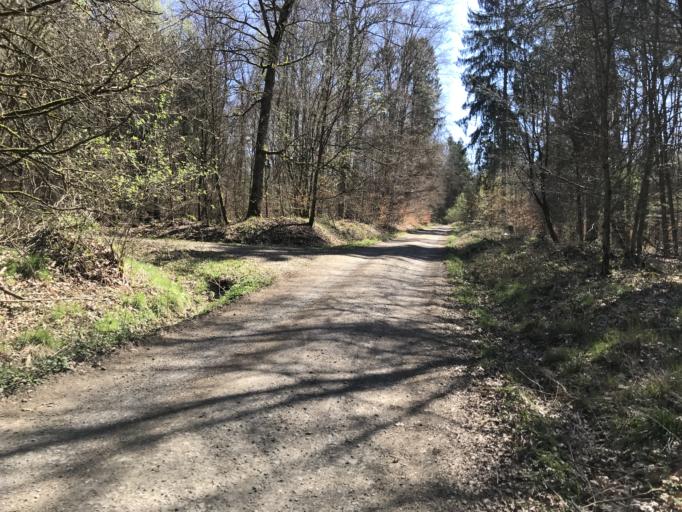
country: DE
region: Hesse
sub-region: Regierungsbezirk Giessen
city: Alten Buseck
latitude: 50.6440
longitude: 8.7521
